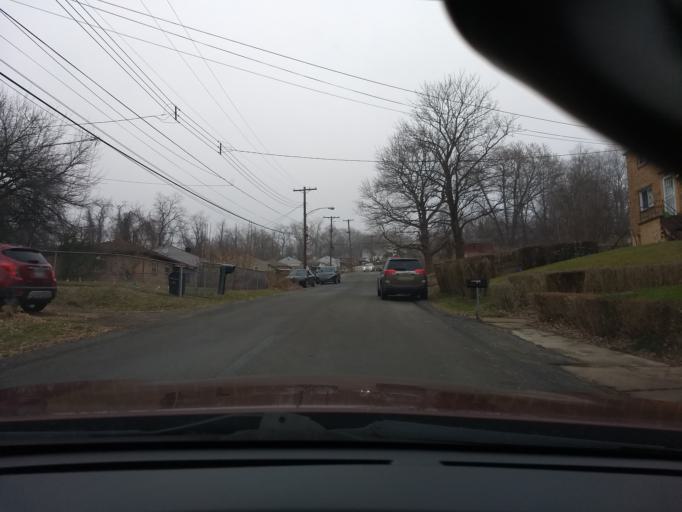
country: US
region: Pennsylvania
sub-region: Allegheny County
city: East Pittsburgh
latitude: 40.3875
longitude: -79.8431
